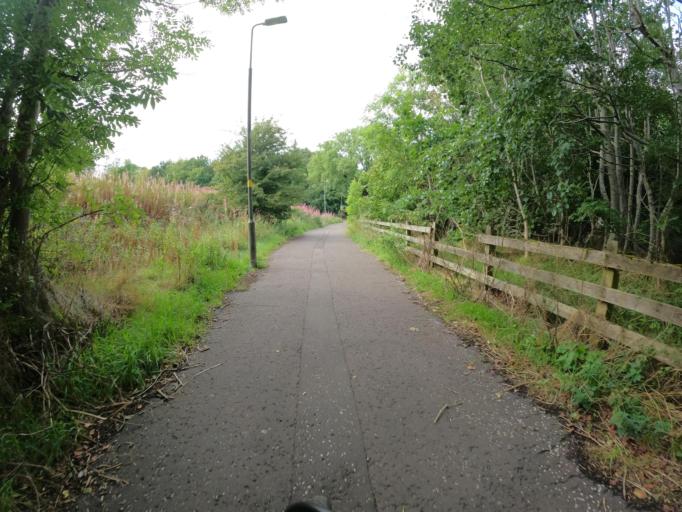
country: GB
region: Scotland
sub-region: West Lothian
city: Livingston
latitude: 55.8660
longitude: -3.5142
